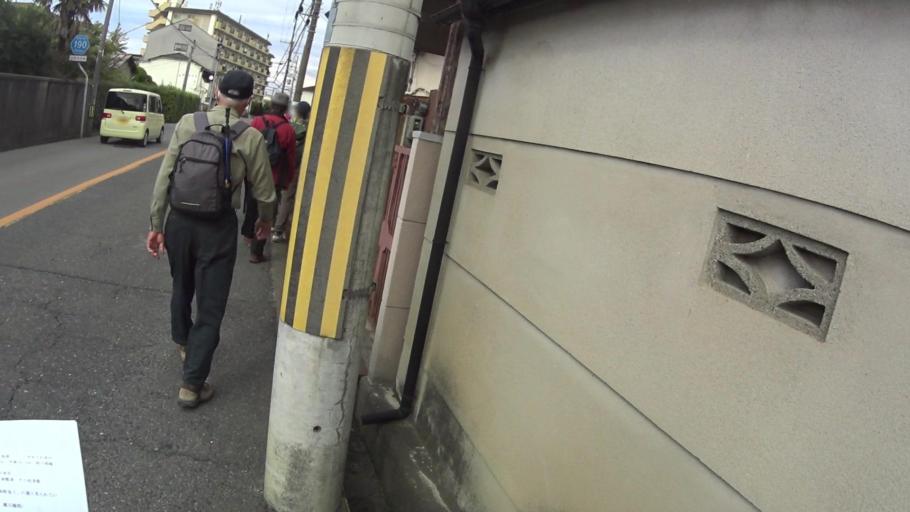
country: JP
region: Osaka
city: Kashihara
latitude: 34.5596
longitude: 135.5925
